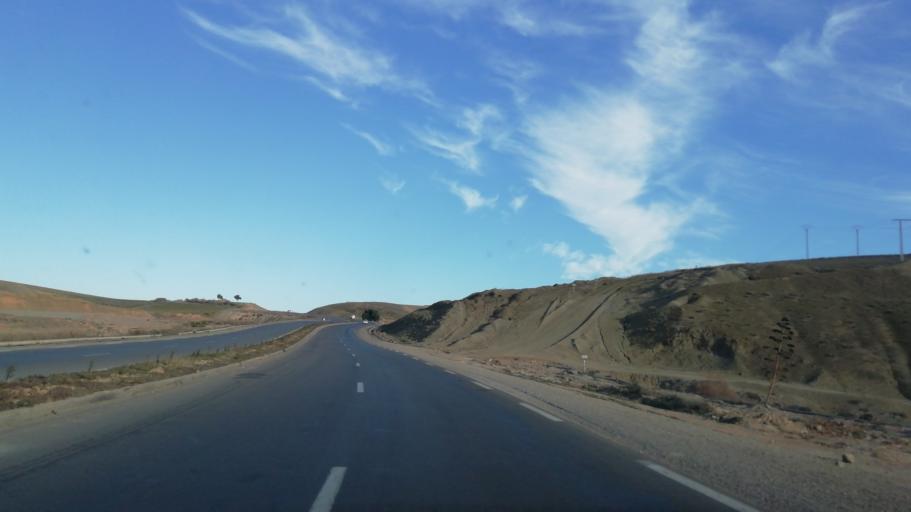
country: DZ
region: Mascara
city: Bou Hanifia el Hamamat
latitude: 35.3313
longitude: 0.0119
